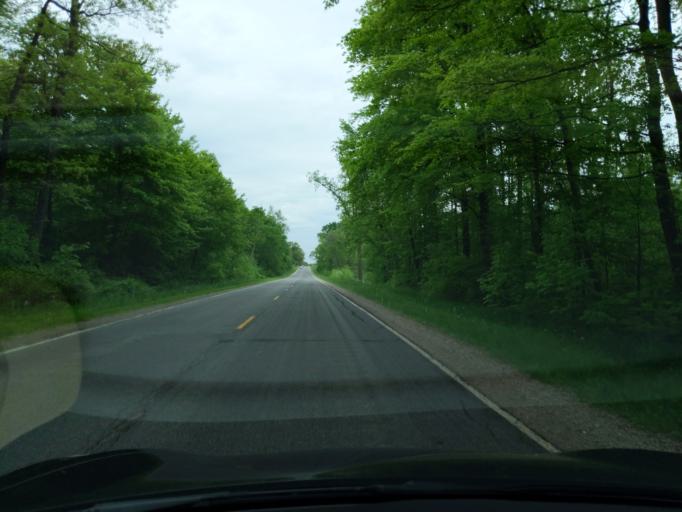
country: US
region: Michigan
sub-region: Ingham County
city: Mason
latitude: 42.5348
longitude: -84.3565
